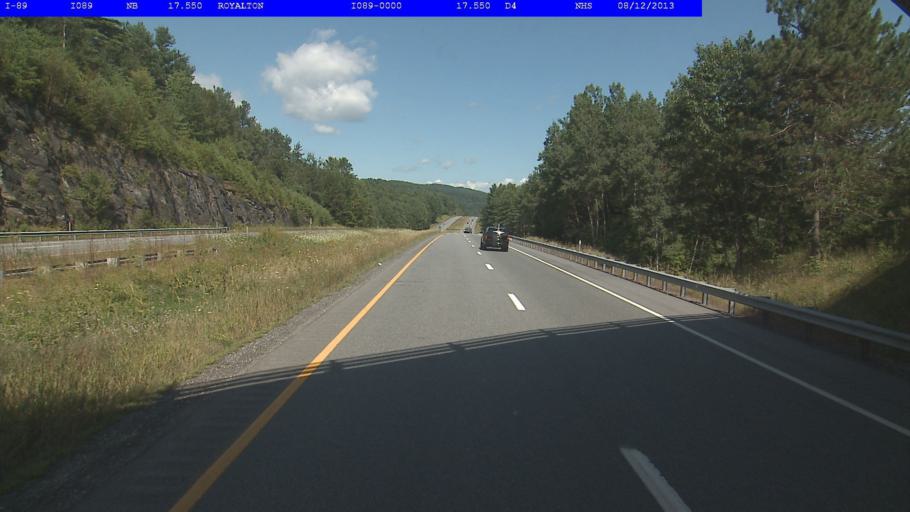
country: US
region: Vermont
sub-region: Windsor County
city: Woodstock
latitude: 43.8079
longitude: -72.5176
